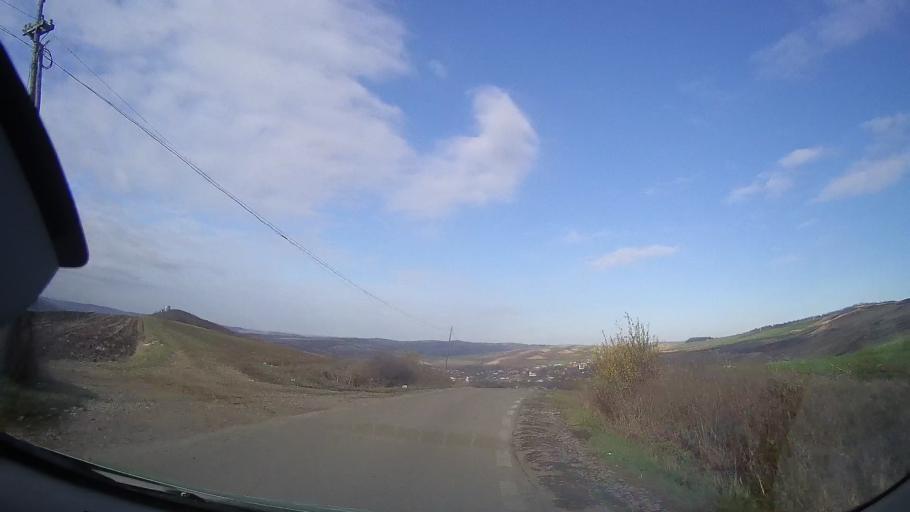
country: RO
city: Barza
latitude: 46.5459
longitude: 24.1475
